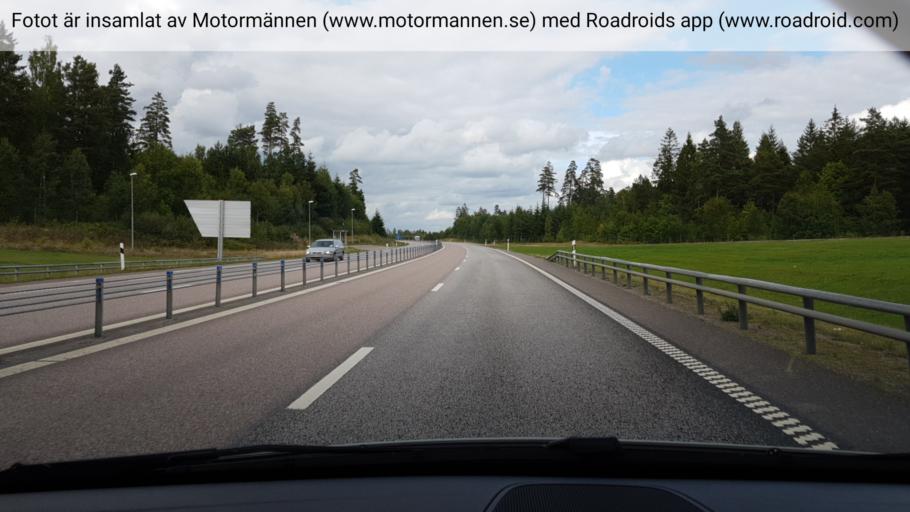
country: SE
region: Vaestra Goetaland
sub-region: Skovde Kommun
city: Skultorp
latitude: 58.3401
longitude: 13.8640
